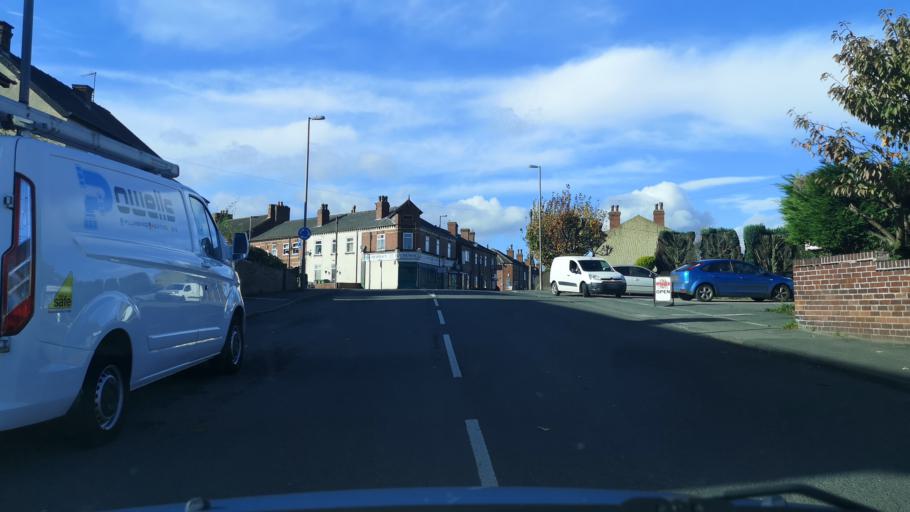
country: GB
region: England
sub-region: City and Borough of Wakefield
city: Normanton
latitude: 53.7043
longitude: -1.4291
